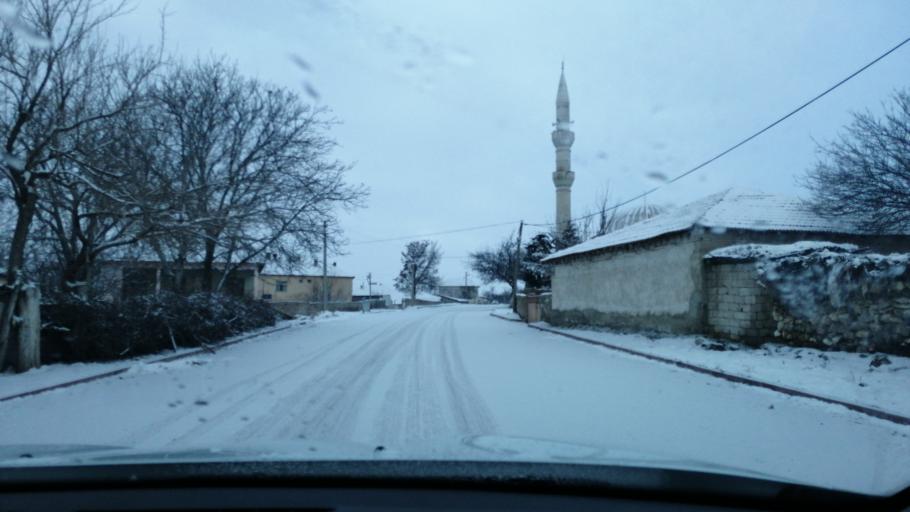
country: TR
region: Aksaray
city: Agacoren
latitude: 38.9342
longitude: 33.9490
